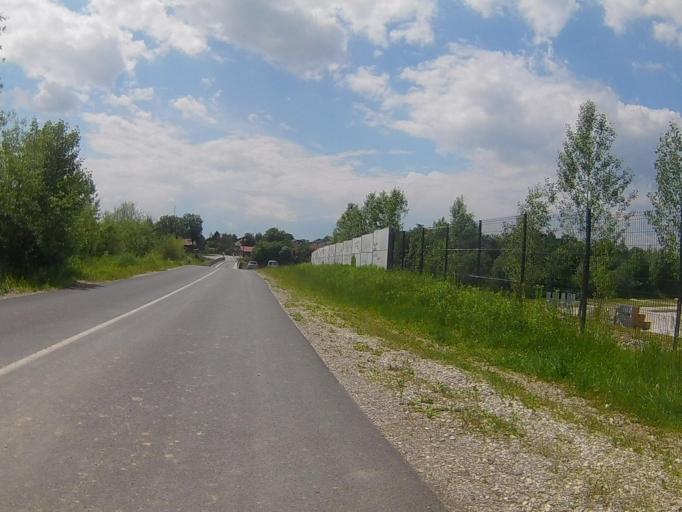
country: SI
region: Kidricevo
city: Kidricevo
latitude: 46.4447
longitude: 15.8143
